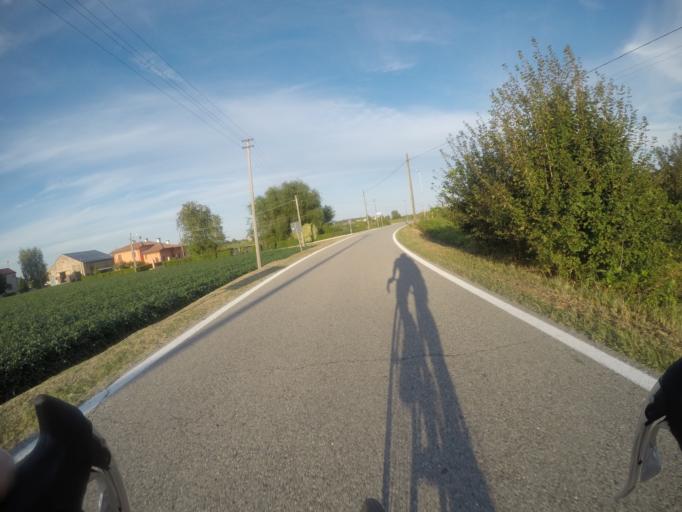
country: IT
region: Veneto
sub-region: Provincia di Rovigo
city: San Bellino
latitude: 45.0190
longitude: 11.5653
